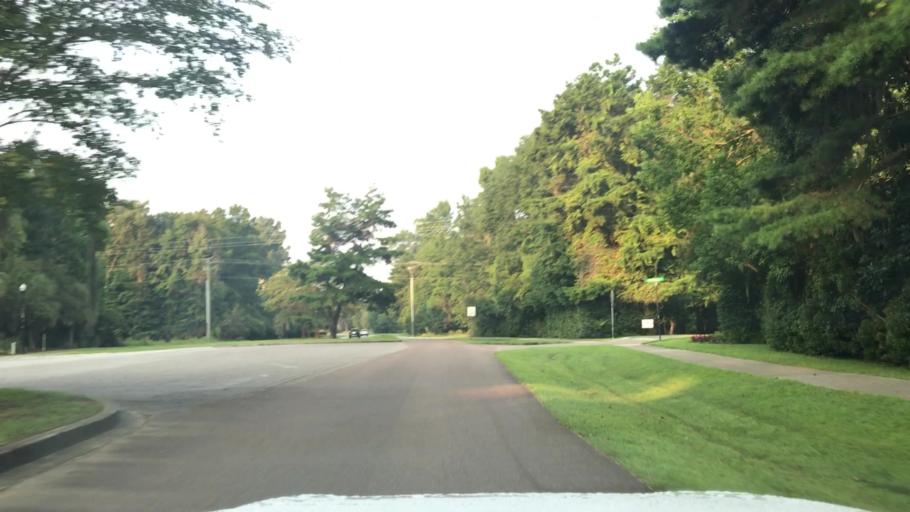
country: US
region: South Carolina
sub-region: Charleston County
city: Shell Point
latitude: 32.8384
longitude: -80.0877
